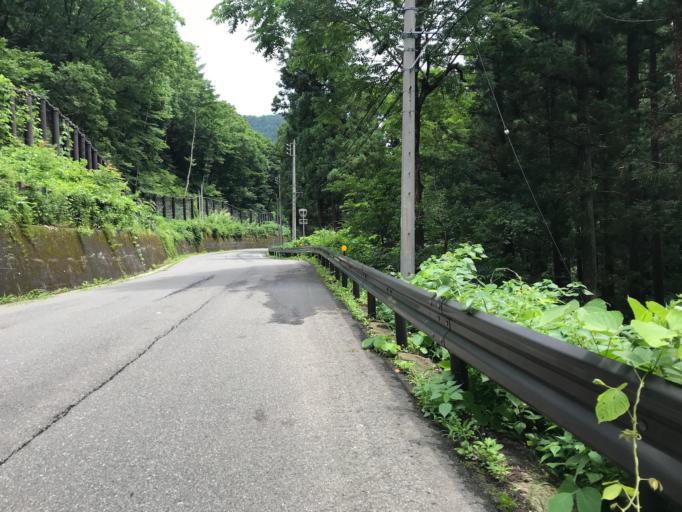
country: JP
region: Gunma
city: Numata
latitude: 36.8209
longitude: 138.9793
